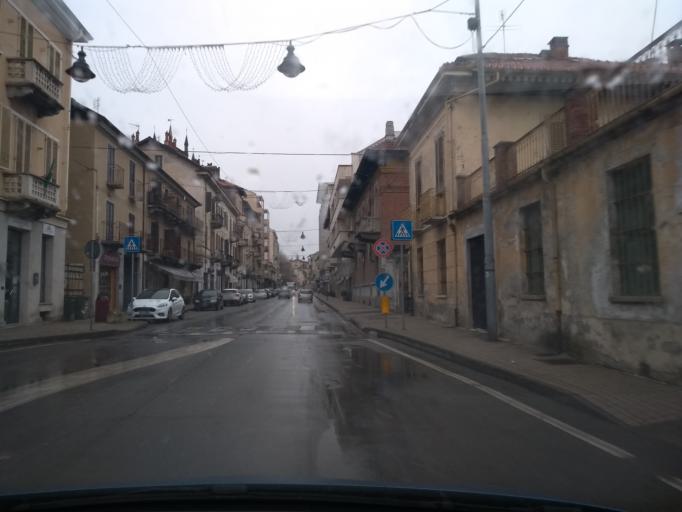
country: IT
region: Piedmont
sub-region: Provincia di Torino
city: Cuorgne
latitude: 45.3897
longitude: 7.6530
